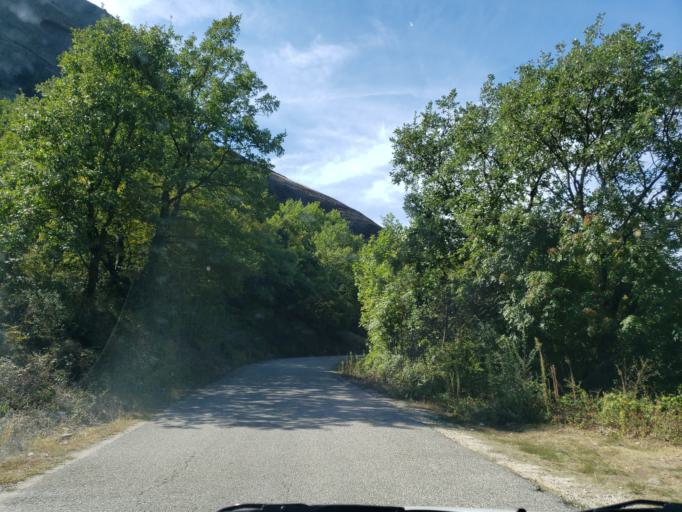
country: GR
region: Thessaly
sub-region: Trikala
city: Kastraki
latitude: 39.7126
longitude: 21.6188
